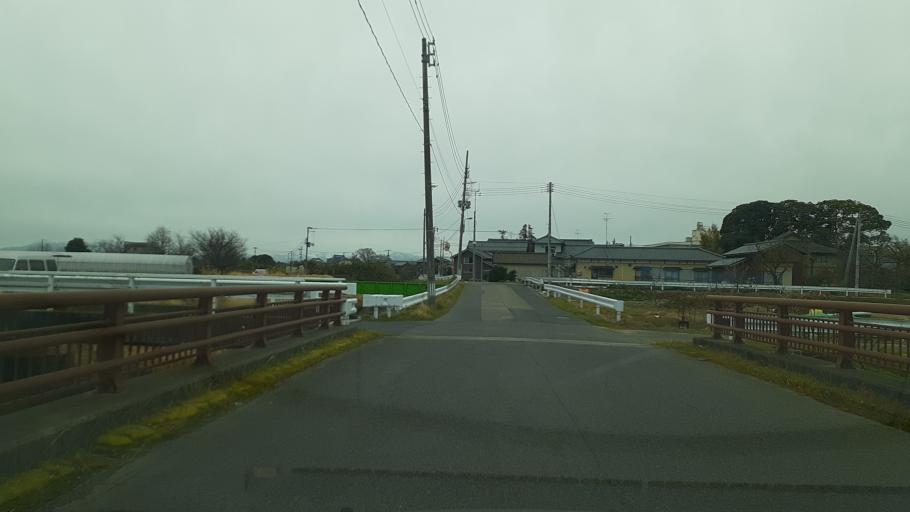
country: JP
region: Niigata
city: Niigata-shi
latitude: 37.8754
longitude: 139.0609
